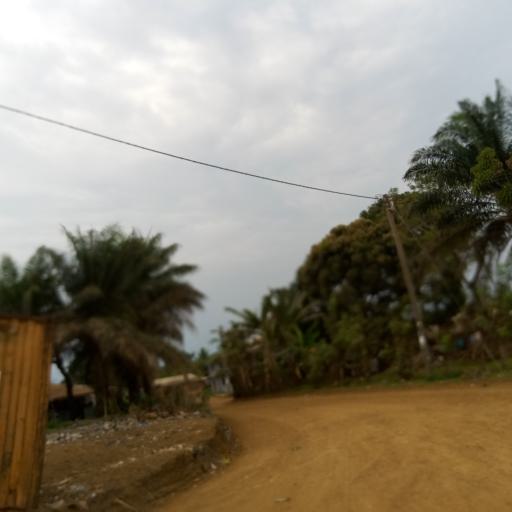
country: LR
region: Montserrado
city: Monrovia
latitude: 6.2940
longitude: -10.6784
